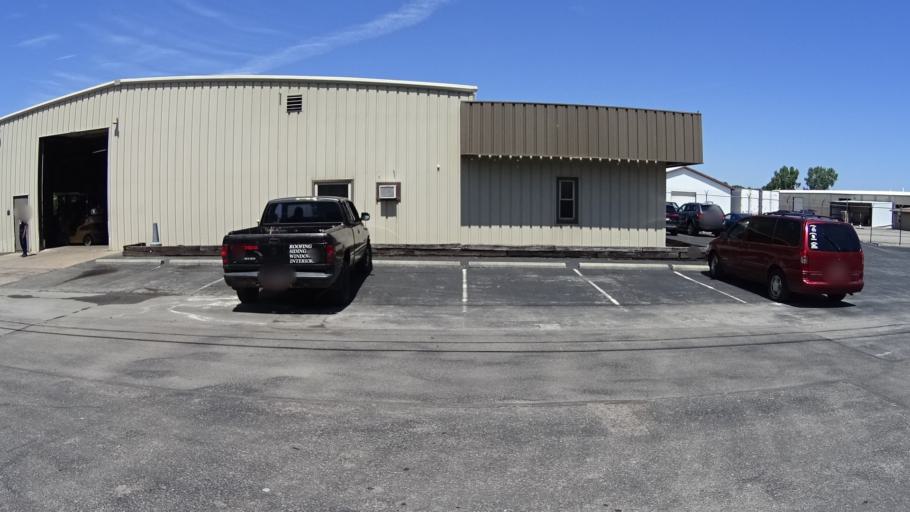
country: US
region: Ohio
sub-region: Erie County
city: Sandusky
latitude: 41.4021
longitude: -82.6840
